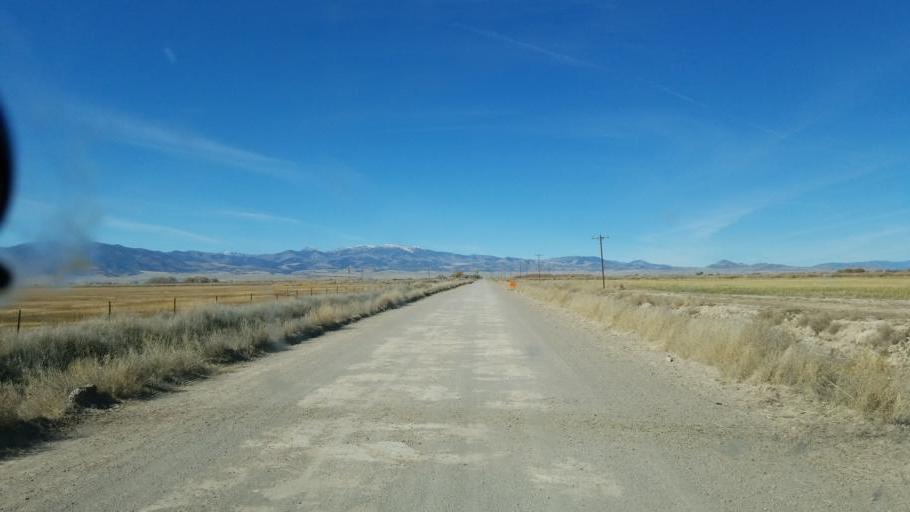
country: US
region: Colorado
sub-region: Rio Grande County
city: Monte Vista
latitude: 37.5313
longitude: -106.0701
